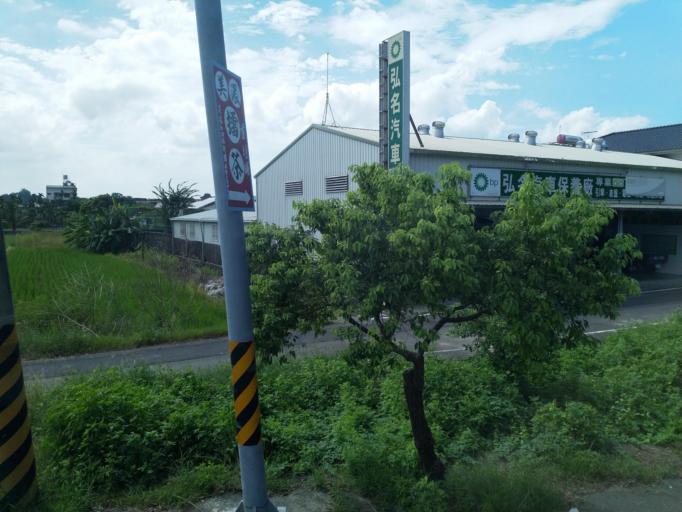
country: TW
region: Taiwan
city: Yujing
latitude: 22.9040
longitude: 120.5536
